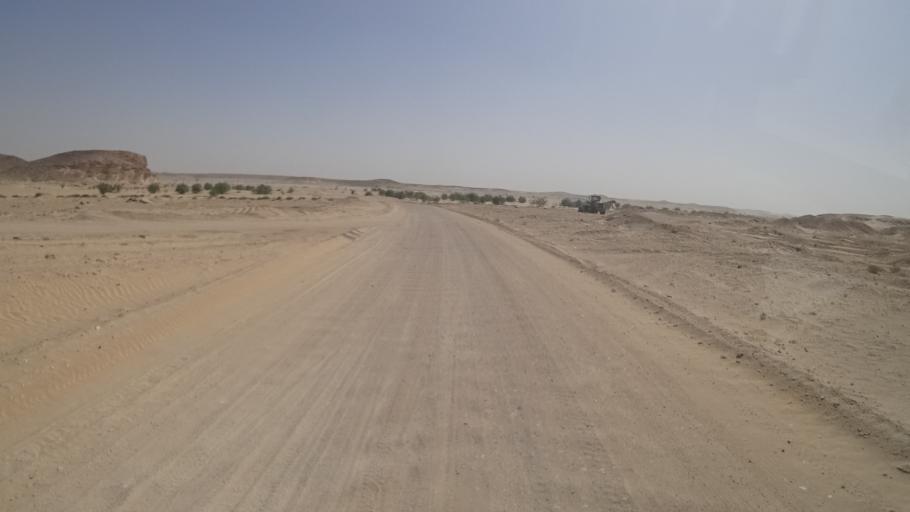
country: YE
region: Al Mahrah
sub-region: Shahan
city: Shihan as Sufla
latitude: 17.8789
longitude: 52.6045
